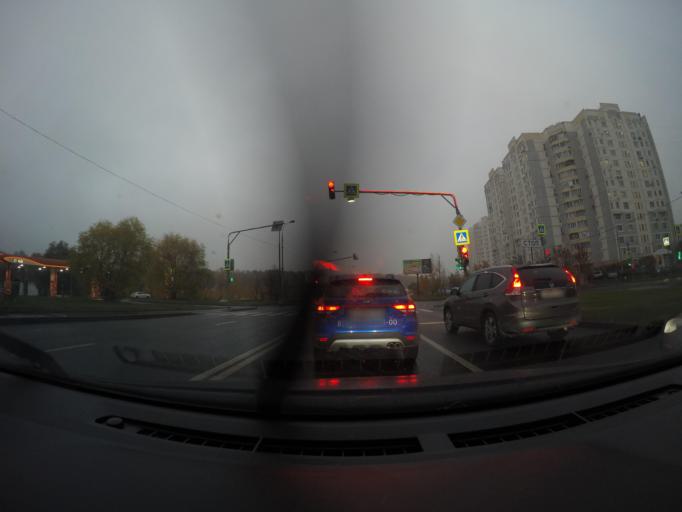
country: RU
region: Moskovskaya
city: Kommunarka
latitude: 55.5515
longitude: 37.5335
